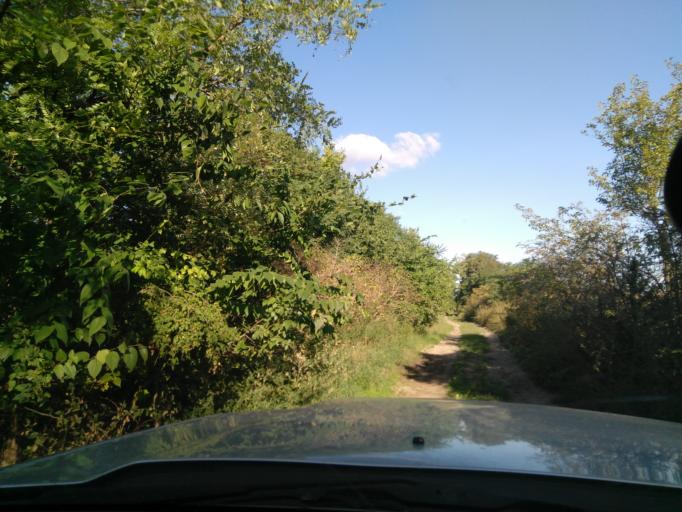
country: HU
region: Fejer
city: Kapolnasnyek
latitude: 47.2676
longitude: 18.7120
